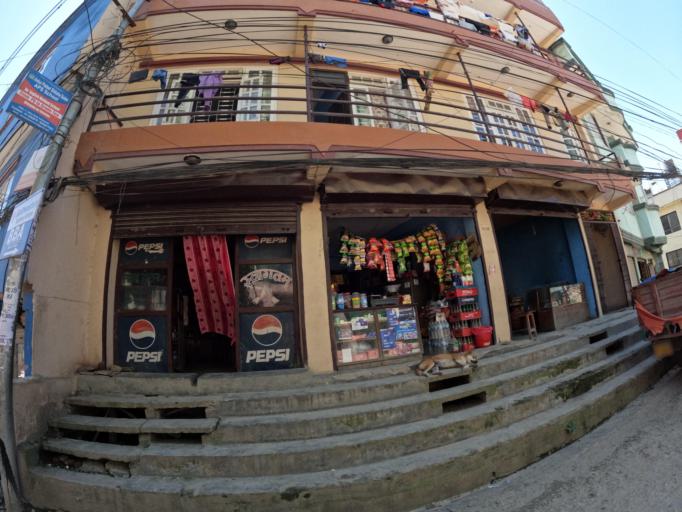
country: NP
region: Central Region
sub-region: Bagmati Zone
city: Kathmandu
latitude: 27.7393
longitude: 85.3238
